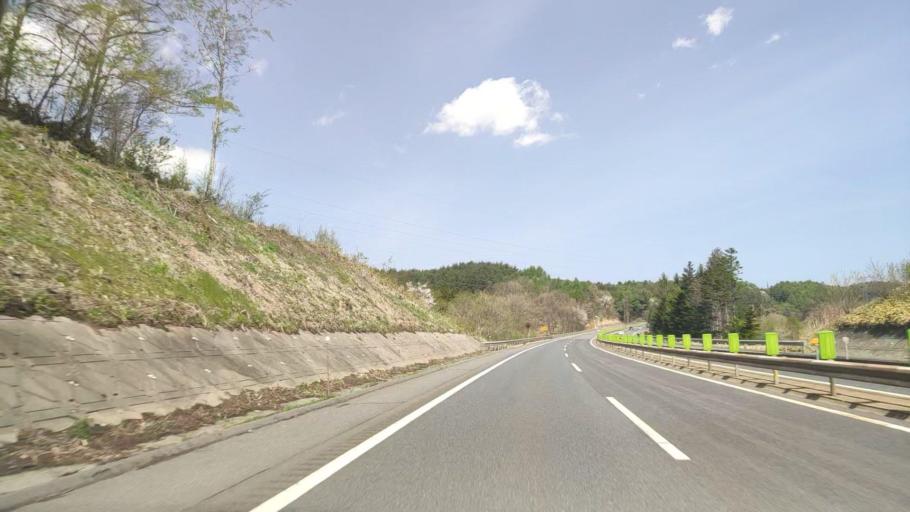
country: JP
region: Aomori
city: Hachinohe
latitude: 40.4214
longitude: 141.4393
